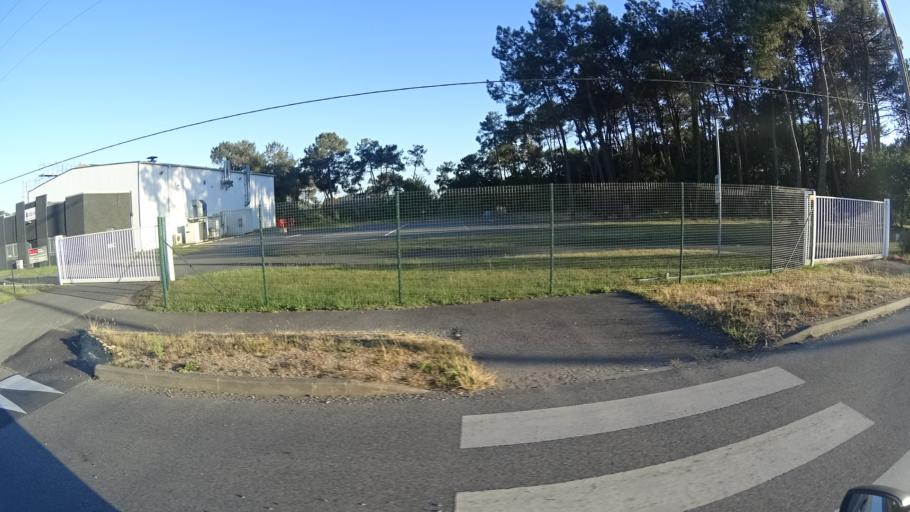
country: FR
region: Brittany
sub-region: Departement d'Ille-et-Vilaine
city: Langon
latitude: 47.7186
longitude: -1.8625
